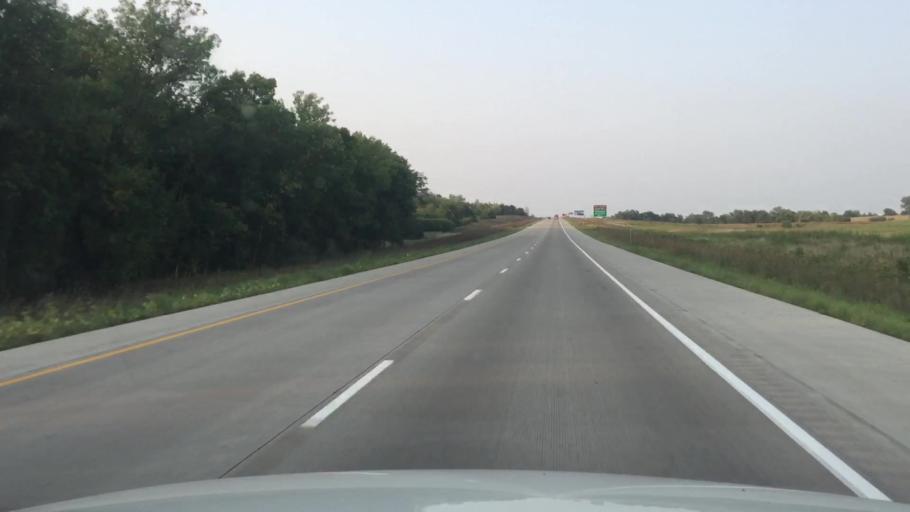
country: US
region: Iowa
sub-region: Decatur County
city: Lamoni
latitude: 40.6101
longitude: -93.9034
